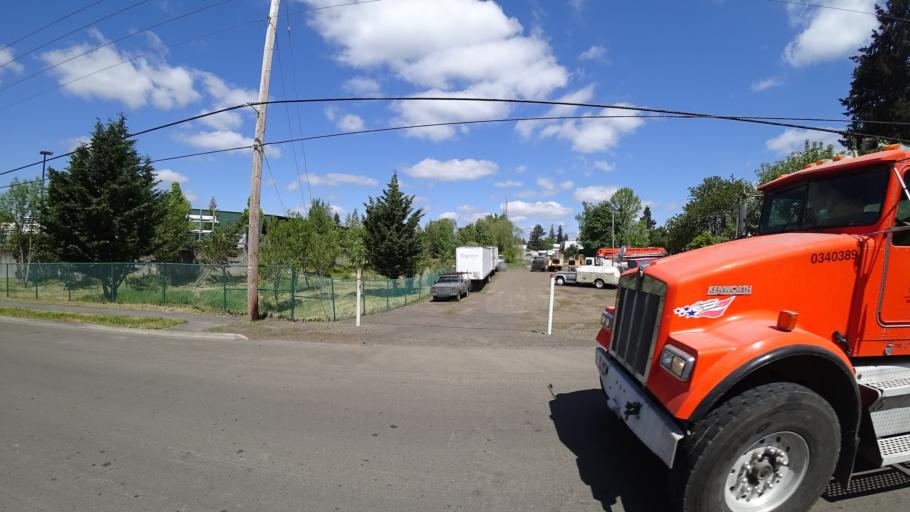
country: US
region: Oregon
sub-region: Washington County
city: Hillsboro
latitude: 45.5128
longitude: -122.9930
